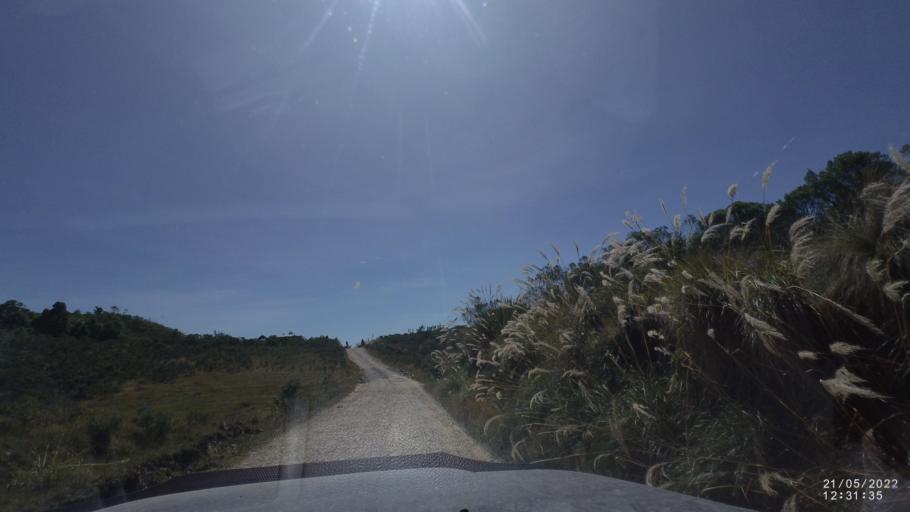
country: BO
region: Cochabamba
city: Colomi
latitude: -17.2107
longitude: -65.9144
